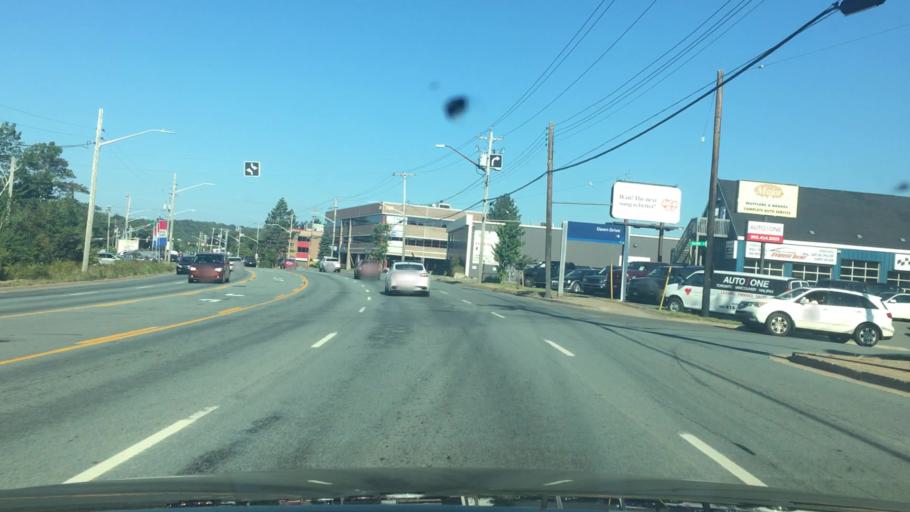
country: CA
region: Nova Scotia
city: Dartmouth
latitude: 44.7022
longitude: -63.6082
